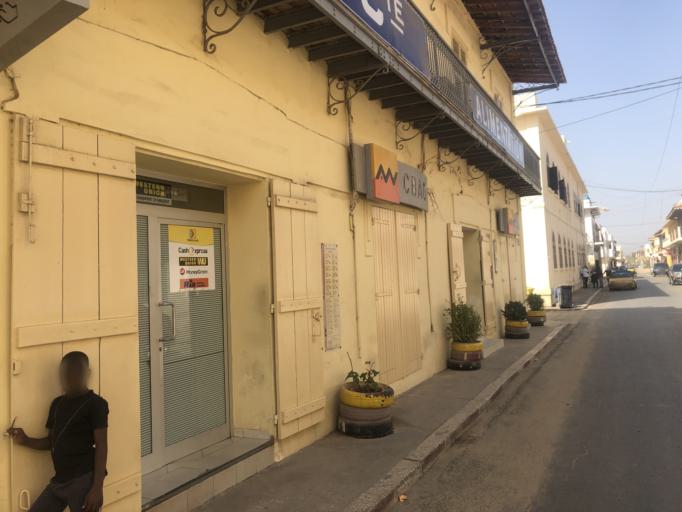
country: SN
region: Saint-Louis
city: Saint-Louis
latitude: 16.0277
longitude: -16.5047
